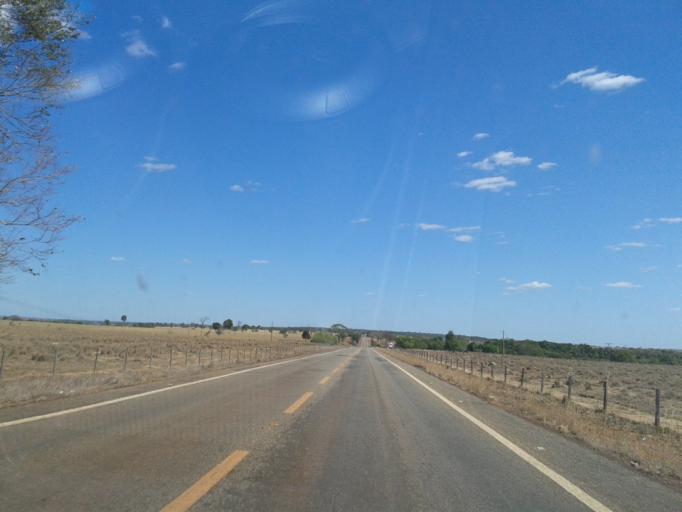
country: BR
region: Goias
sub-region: Sao Miguel Do Araguaia
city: Sao Miguel do Araguaia
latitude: -13.4342
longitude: -50.2837
